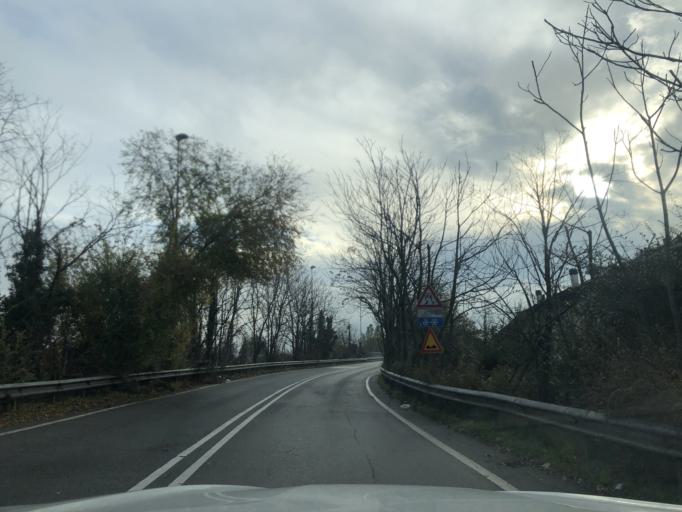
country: IT
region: Lombardy
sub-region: Citta metropolitana di Milano
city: Cologno Monzese
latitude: 45.5534
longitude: 9.2647
